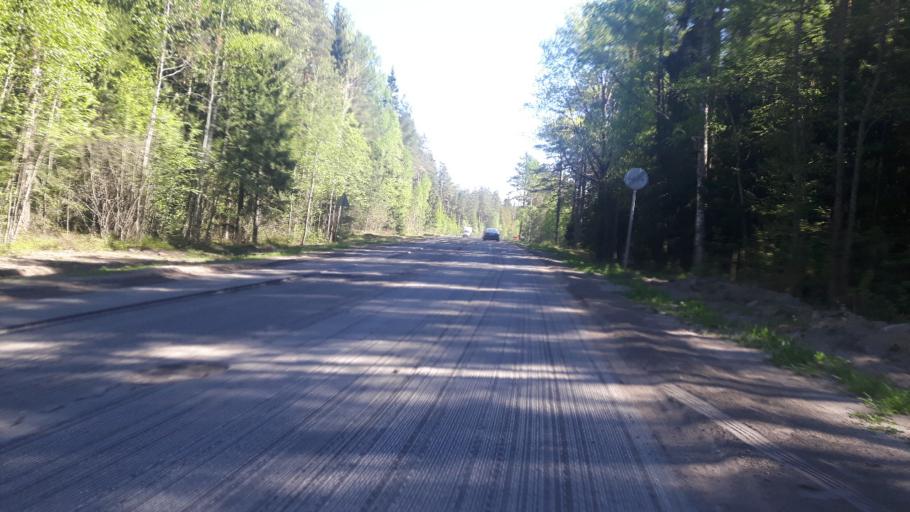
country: RU
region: Leningrad
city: Sosnovyy Bor
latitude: 60.2286
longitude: 29.0025
